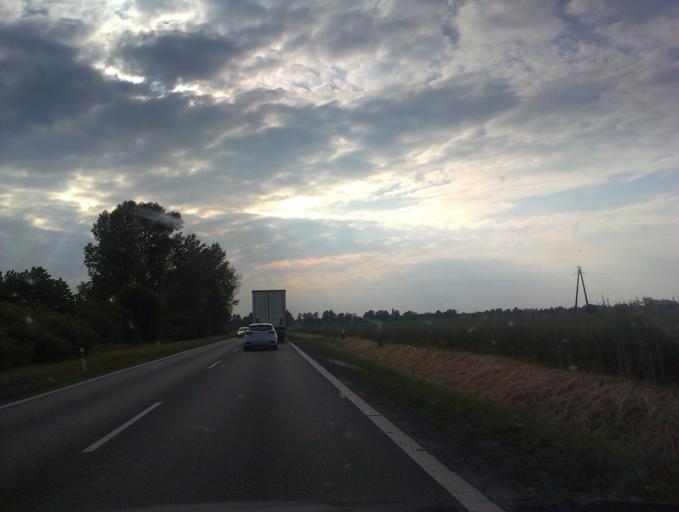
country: PL
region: Lower Silesian Voivodeship
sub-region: Powiat trzebnicki
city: Prusice
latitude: 51.3615
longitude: 16.9874
